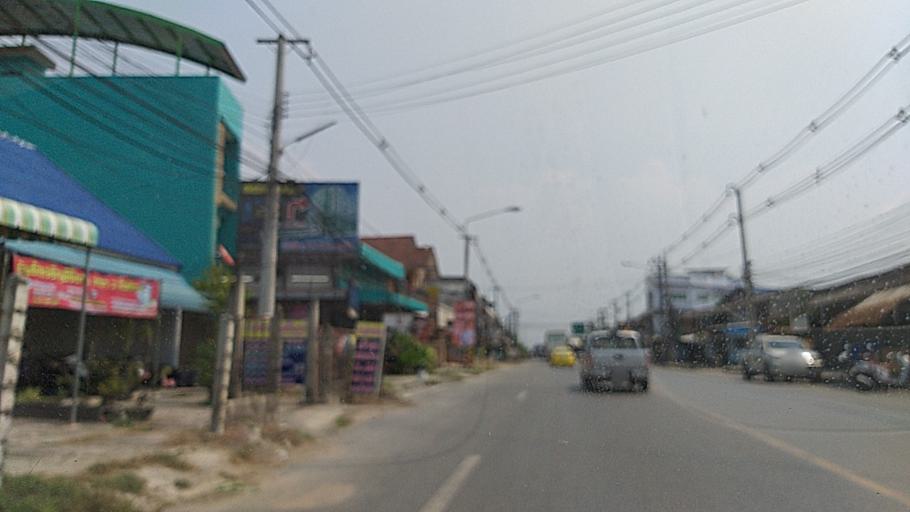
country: TH
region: Chon Buri
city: Phanat Nikhom
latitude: 13.4385
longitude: 101.1793
